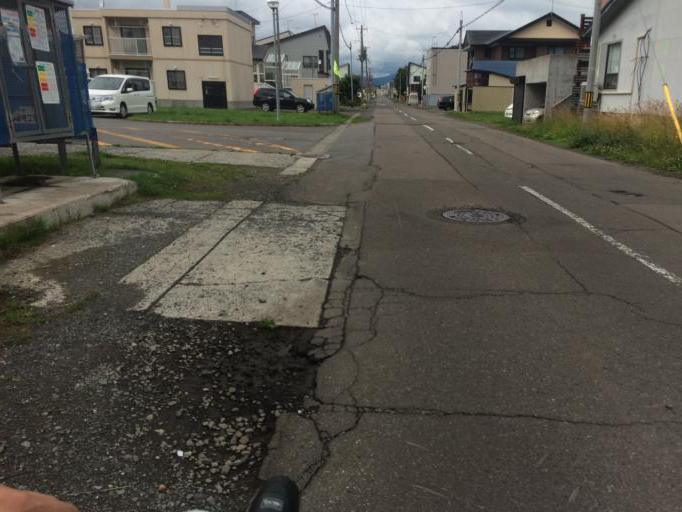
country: JP
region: Hokkaido
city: Niseko Town
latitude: 42.8904
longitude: 140.7509
